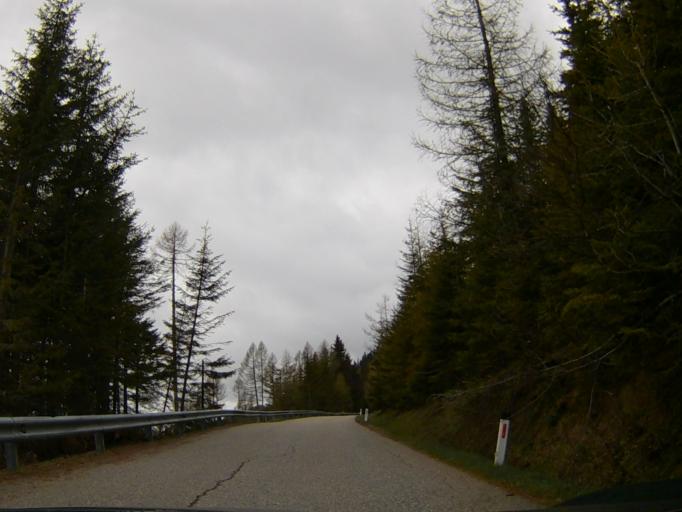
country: AT
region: Carinthia
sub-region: Politischer Bezirk Villach Land
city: Stockenboi
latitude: 46.7504
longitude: 13.4959
